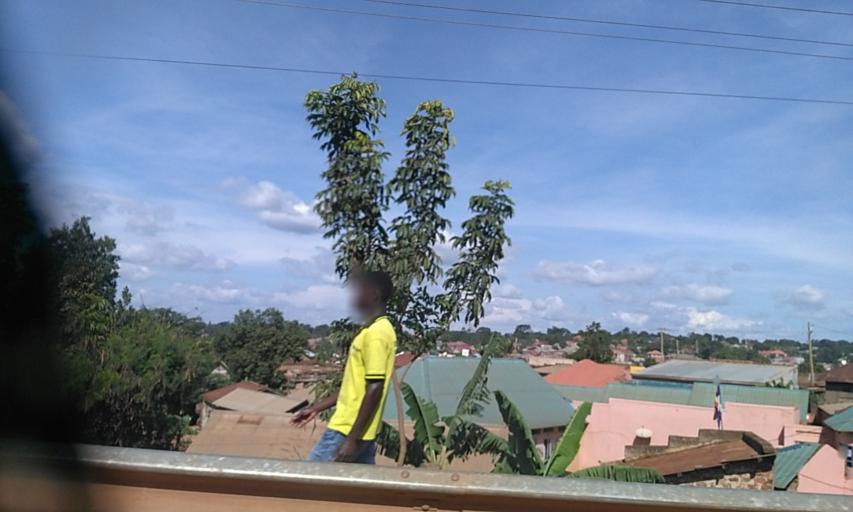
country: UG
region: Central Region
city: Kampala Central Division
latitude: 0.3879
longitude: 32.5527
